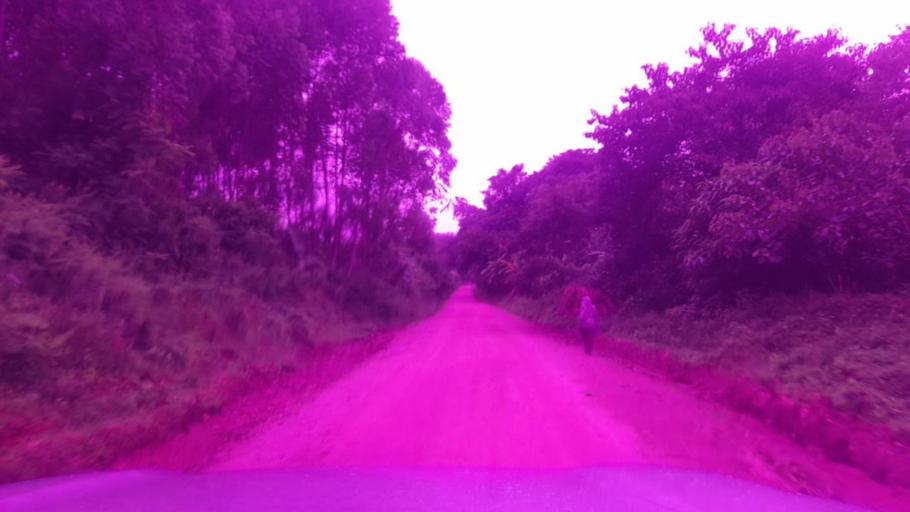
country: ET
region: Southern Nations, Nationalities, and People's Region
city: Bonga
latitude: 7.4626
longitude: 36.1270
